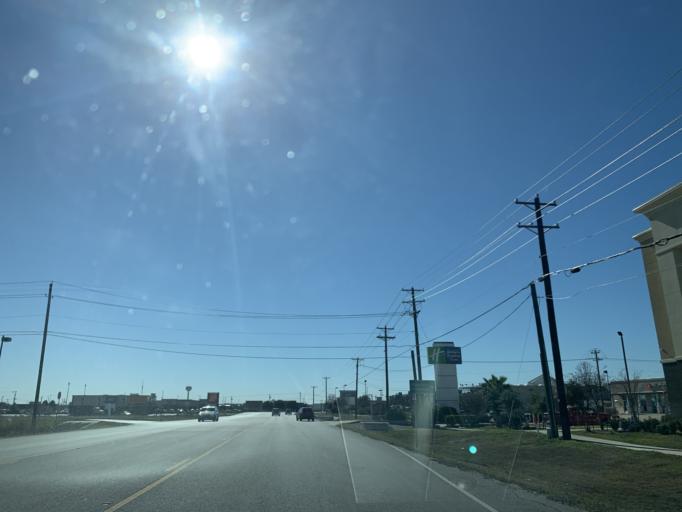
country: US
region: Texas
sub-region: Williamson County
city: Hutto
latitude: 30.5450
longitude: -97.5614
